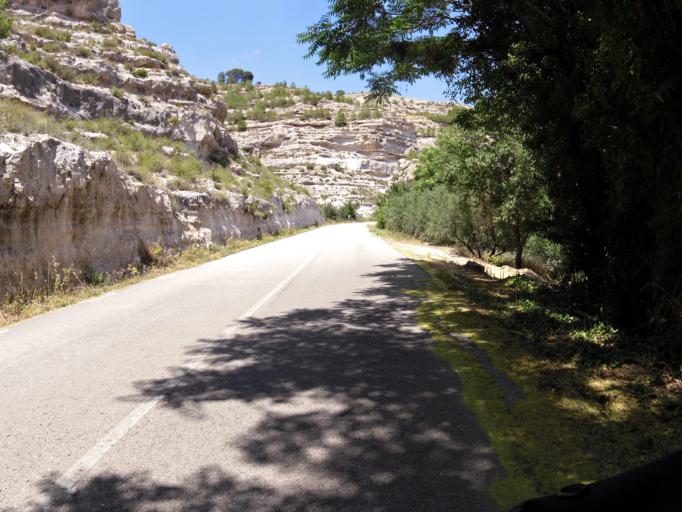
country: ES
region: Castille-La Mancha
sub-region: Provincia de Albacete
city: Jorquera
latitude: 39.1774
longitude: -1.5342
